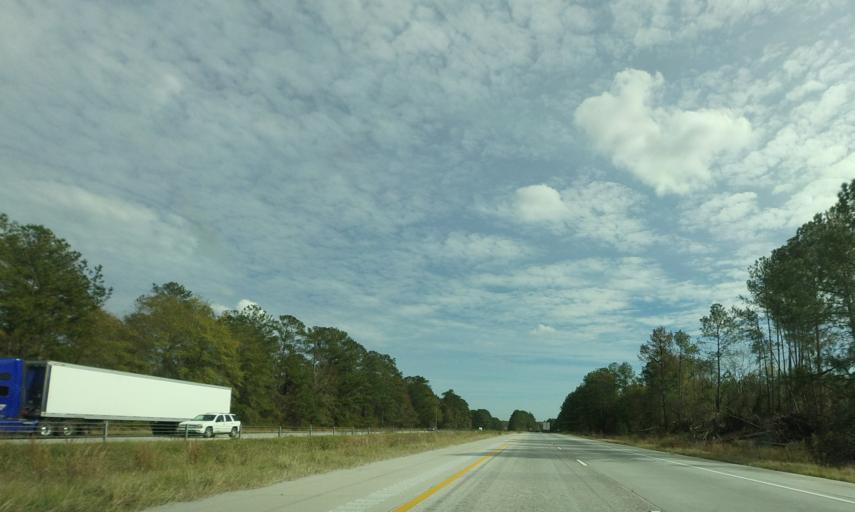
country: US
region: Georgia
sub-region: Laurens County
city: Dublin
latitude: 32.5056
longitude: -83.0252
